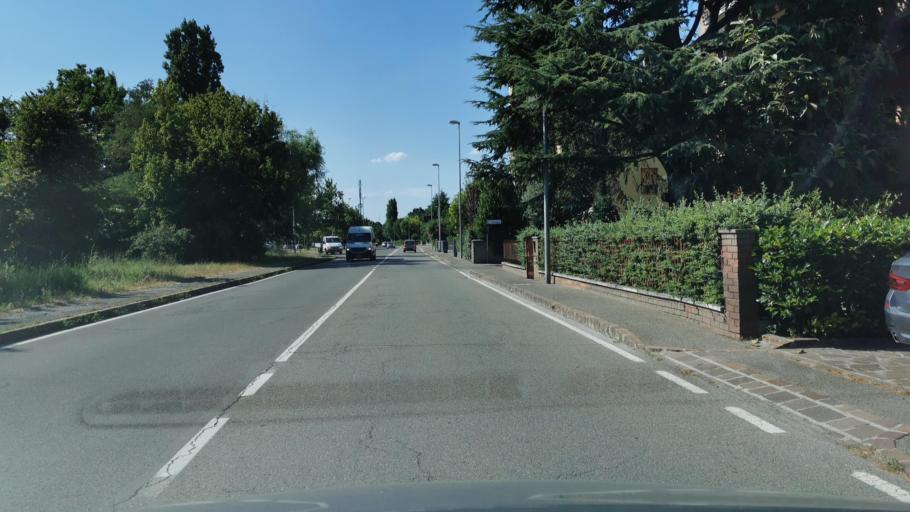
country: IT
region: Emilia-Romagna
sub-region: Provincia di Modena
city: Modena
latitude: 44.6198
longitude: 10.9302
